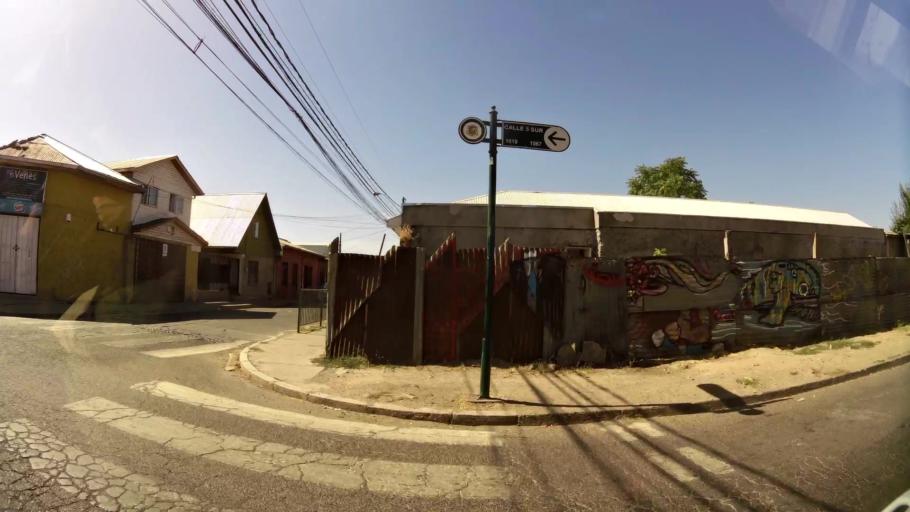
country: CL
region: Maule
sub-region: Provincia de Talca
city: Talca
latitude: -35.4319
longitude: -71.6630
